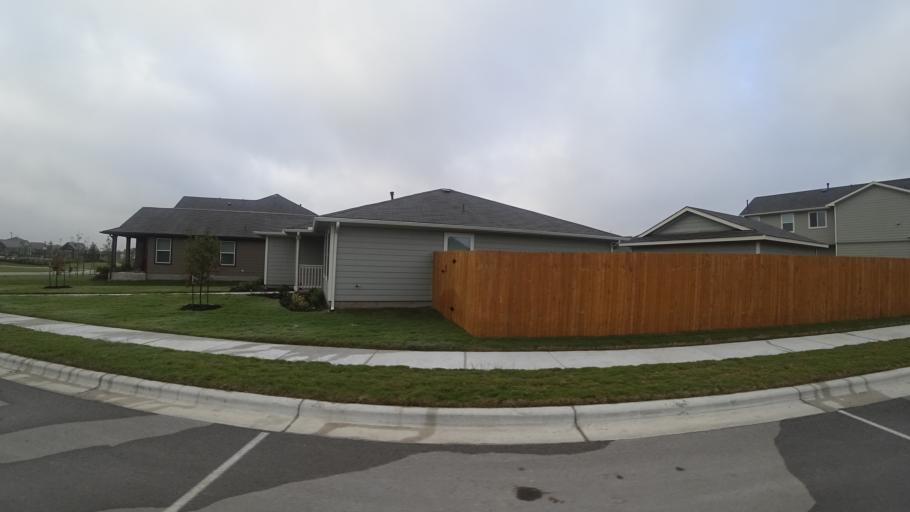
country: US
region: Texas
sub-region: Travis County
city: Wells Branch
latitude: 30.3589
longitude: -97.6672
